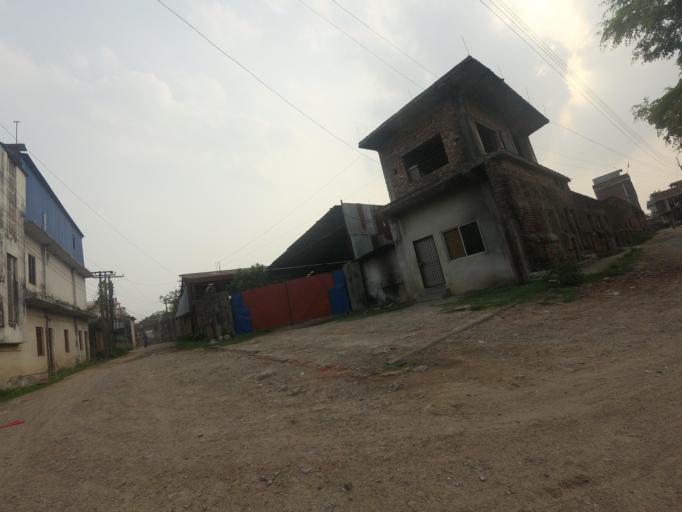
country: NP
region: Western Region
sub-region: Lumbini Zone
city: Bhairahawa
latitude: 27.5095
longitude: 83.4343
